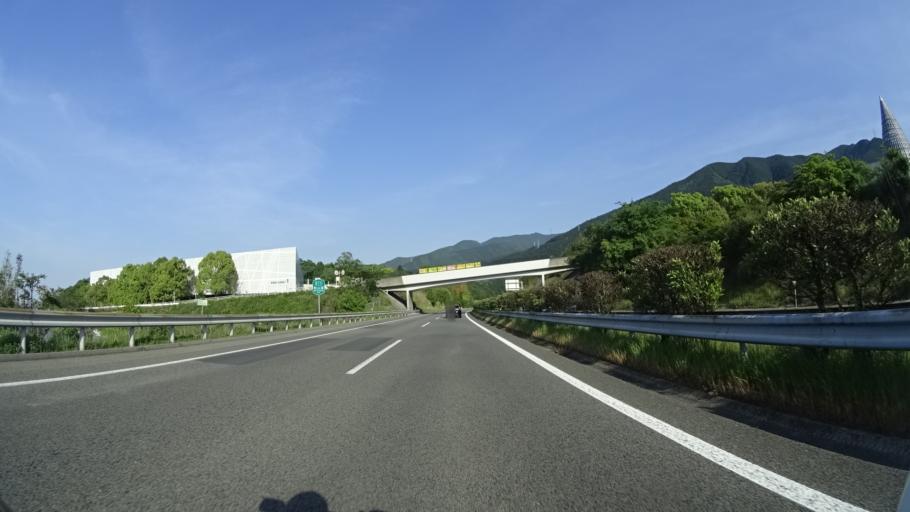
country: JP
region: Ehime
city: Saijo
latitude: 33.9117
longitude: 133.2441
